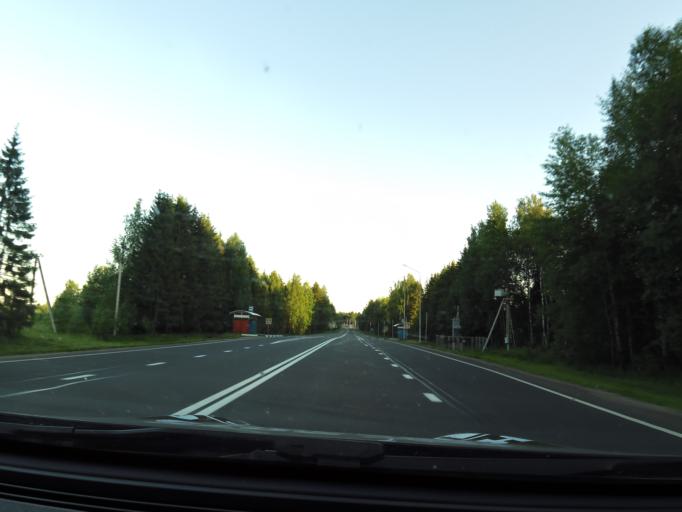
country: RU
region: Jaroslavl
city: Prechistoye
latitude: 58.4672
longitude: 40.3210
